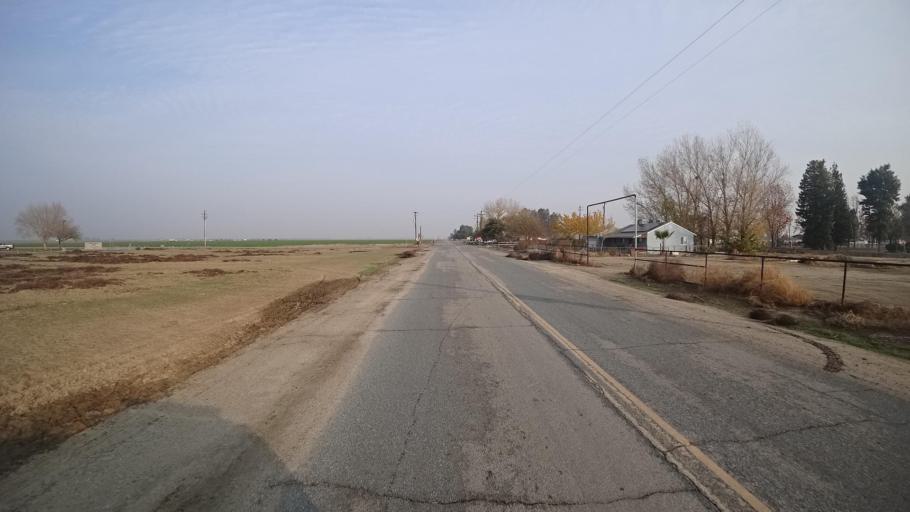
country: US
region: California
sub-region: Kern County
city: Greenfield
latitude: 35.2223
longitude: -119.0215
